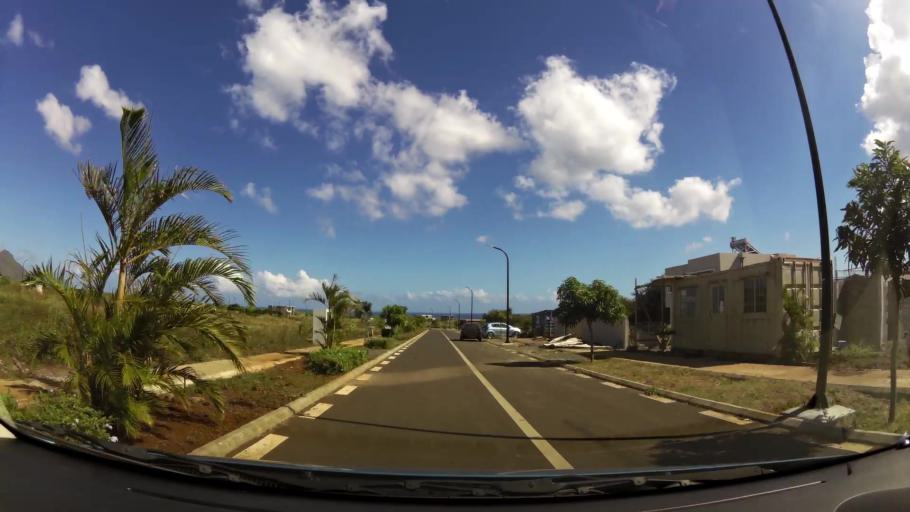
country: MU
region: Black River
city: Cascavelle
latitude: -20.2815
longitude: 57.3910
